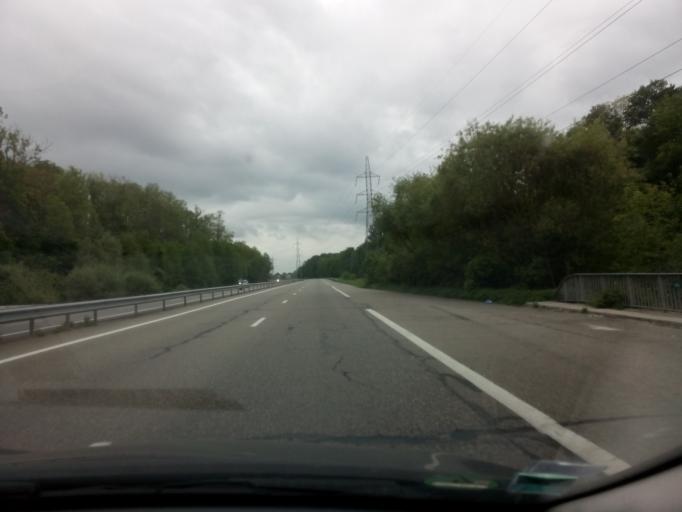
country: FR
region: Alsace
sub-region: Departement du Bas-Rhin
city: Drusenheim
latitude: 48.7604
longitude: 7.9261
